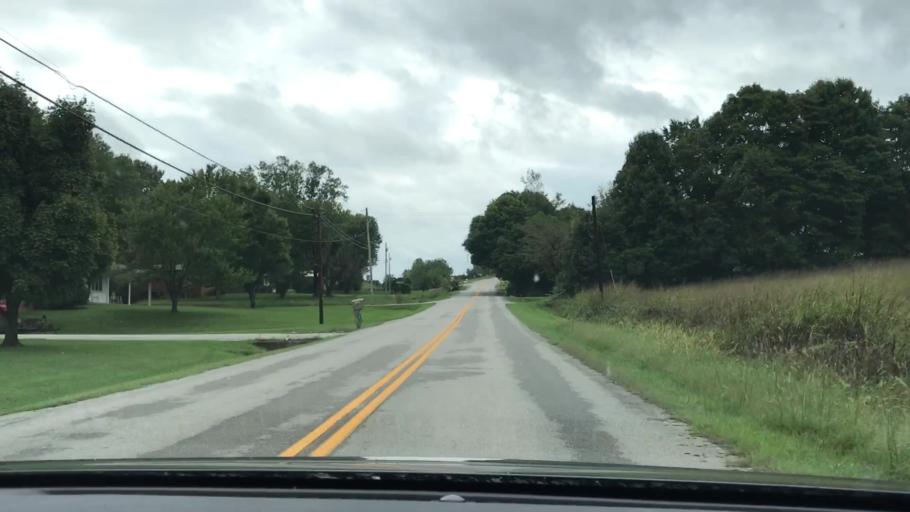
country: US
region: Kentucky
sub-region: Barren County
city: Glasgow
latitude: 36.9603
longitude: -85.8648
